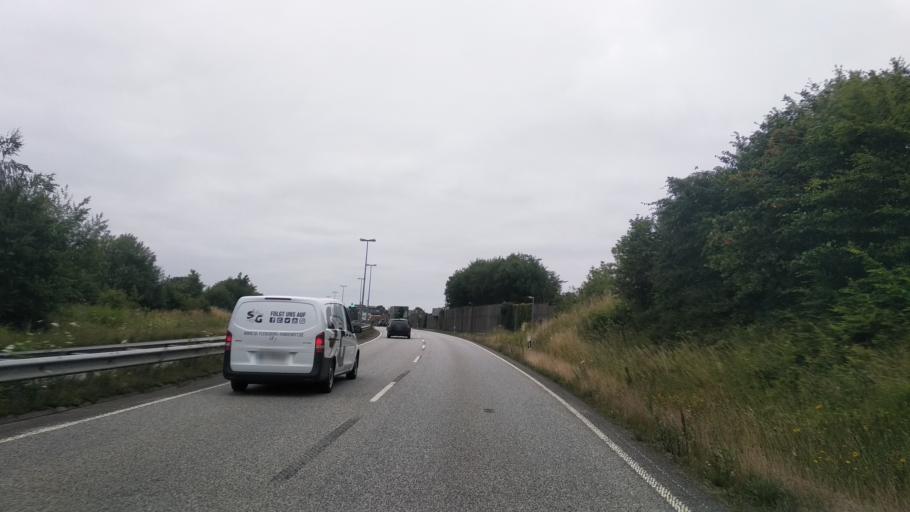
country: DE
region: Schleswig-Holstein
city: Flensburg
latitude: 54.7930
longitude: 9.4659
